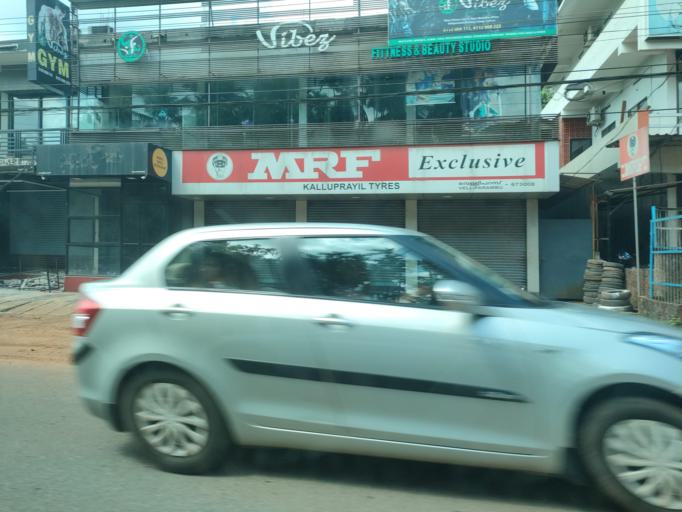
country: IN
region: Kerala
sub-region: Kozhikode
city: Kunnamangalam
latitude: 11.2697
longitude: 75.8523
